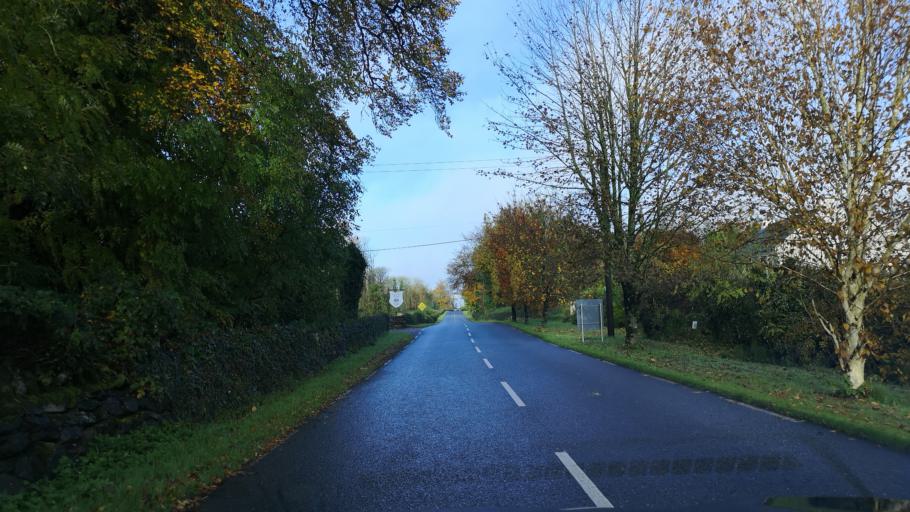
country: IE
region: Leinster
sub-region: An Iarmhi
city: Moate
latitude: 53.3789
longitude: -7.7997
